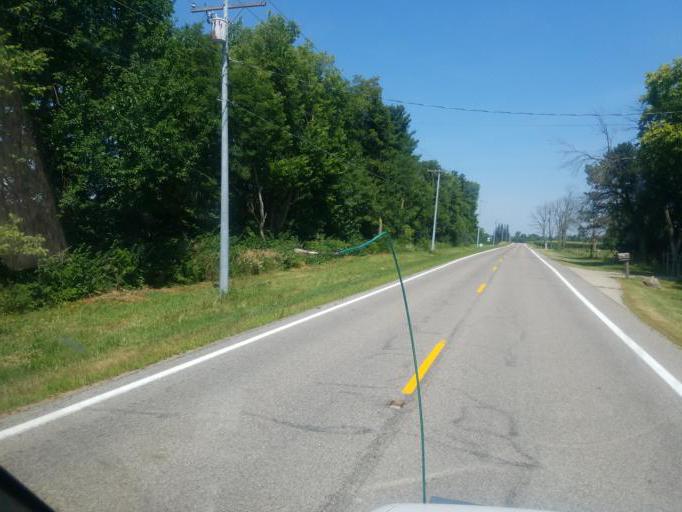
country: US
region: Ohio
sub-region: Champaign County
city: North Lewisburg
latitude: 40.2074
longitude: -83.5386
